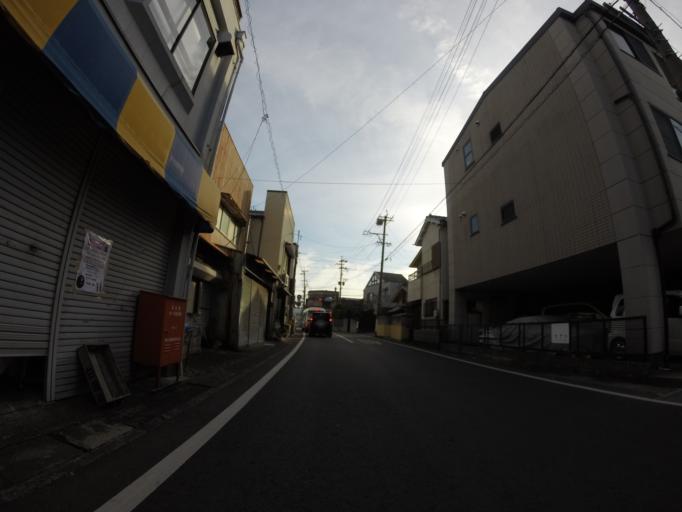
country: JP
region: Shizuoka
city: Shizuoka-shi
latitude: 35.0324
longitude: 138.4830
